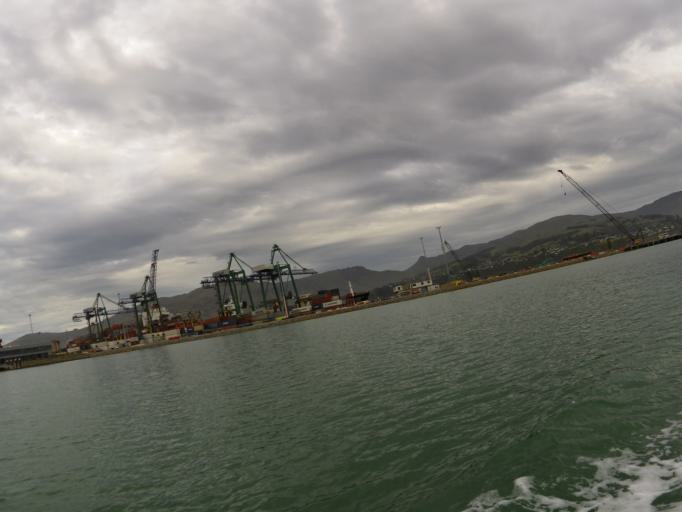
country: NZ
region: Canterbury
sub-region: Christchurch City
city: Christchurch
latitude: -43.6072
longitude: 172.7204
